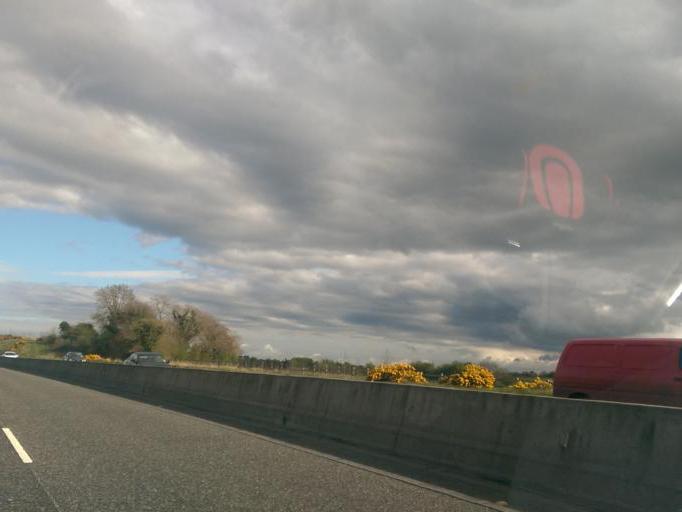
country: IE
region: Leinster
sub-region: Uibh Fhaili
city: Clara
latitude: 53.3874
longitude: -7.6021
